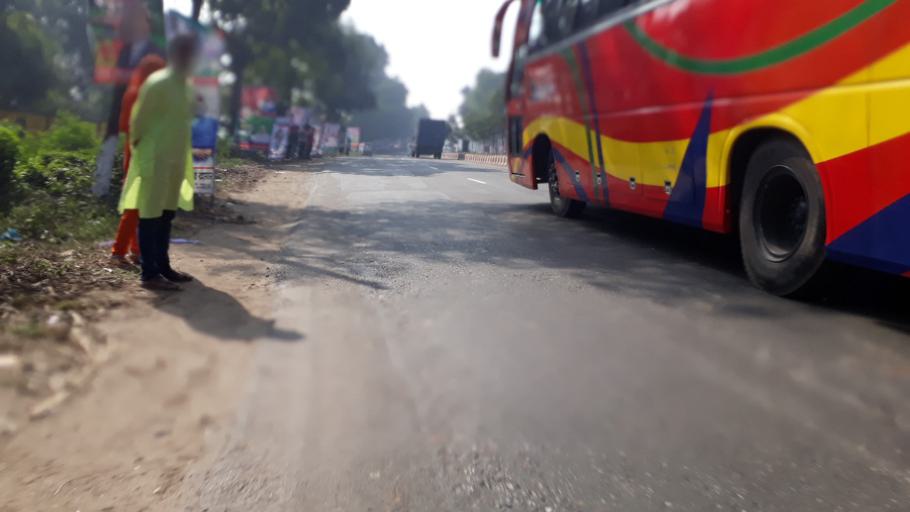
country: BD
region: Dhaka
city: Tungi
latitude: 23.8709
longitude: 90.2731
